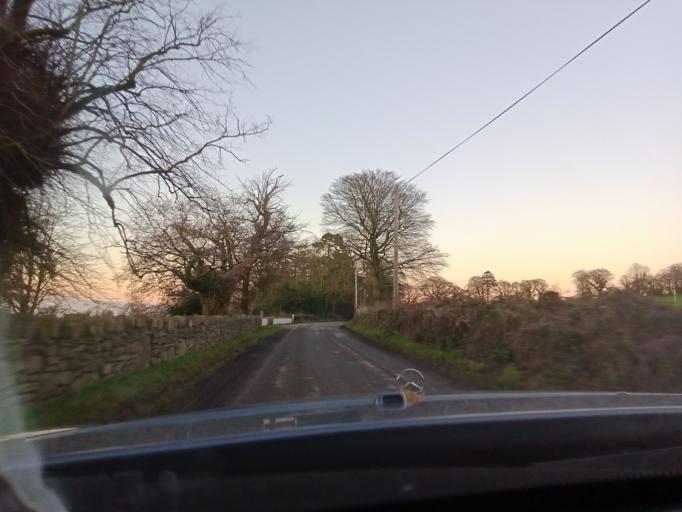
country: IE
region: Leinster
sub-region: Kilkenny
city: Thomastown
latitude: 52.4614
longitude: -7.1020
